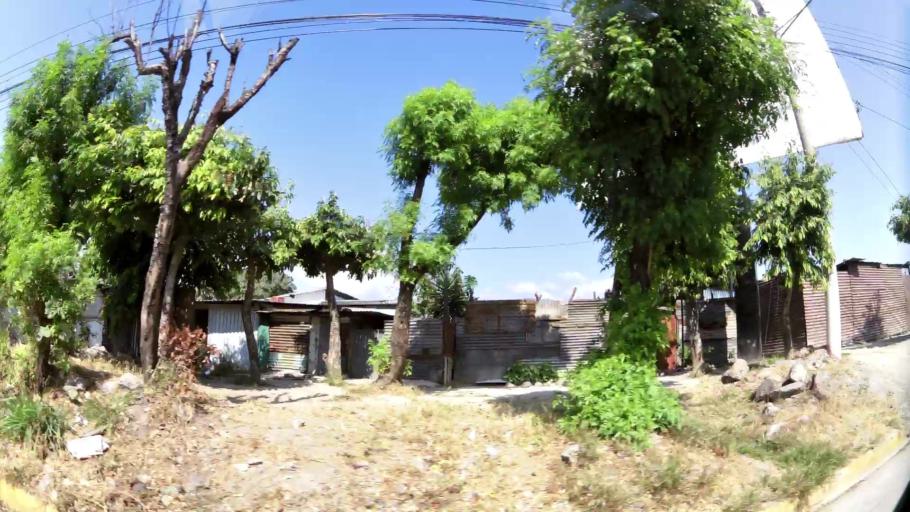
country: SV
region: La Libertad
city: Antiguo Cuscatlan
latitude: 13.6755
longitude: -89.2507
